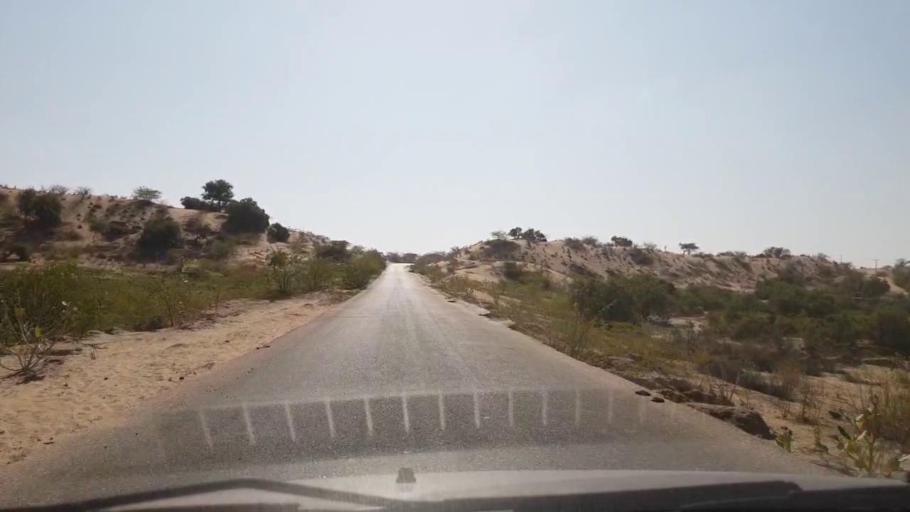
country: PK
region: Sindh
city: Mithi
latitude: 24.5924
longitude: 69.7128
